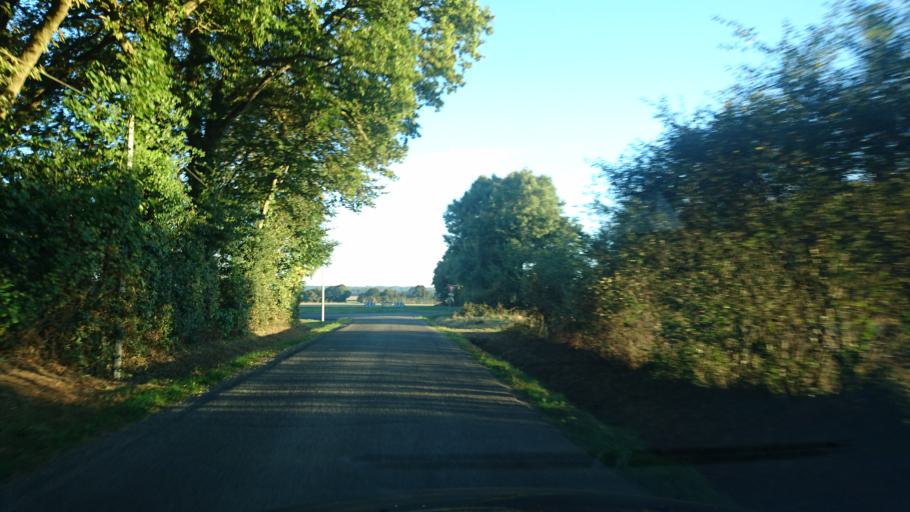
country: FR
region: Brittany
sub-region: Departement d'Ille-et-Vilaine
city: Bains-sur-Oust
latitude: 47.7069
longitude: -2.0353
